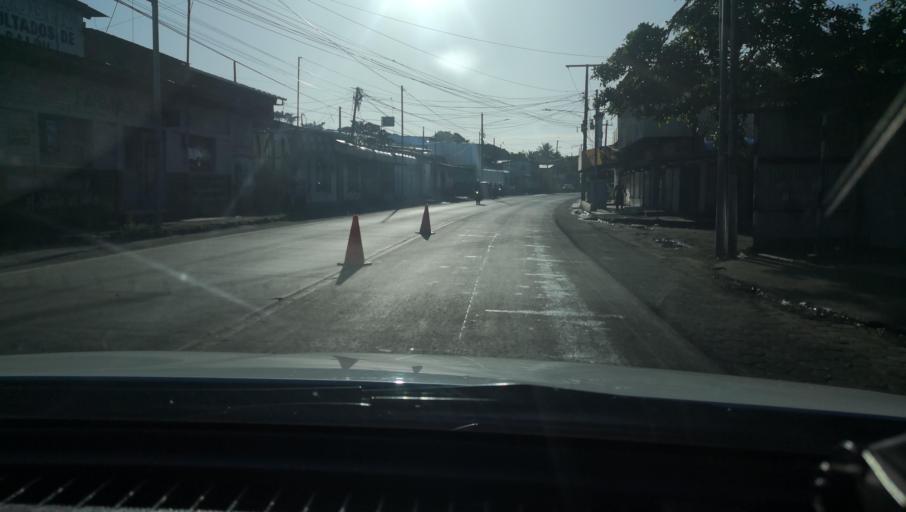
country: NI
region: Carazo
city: Diriamba
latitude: 11.8597
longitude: -86.2353
